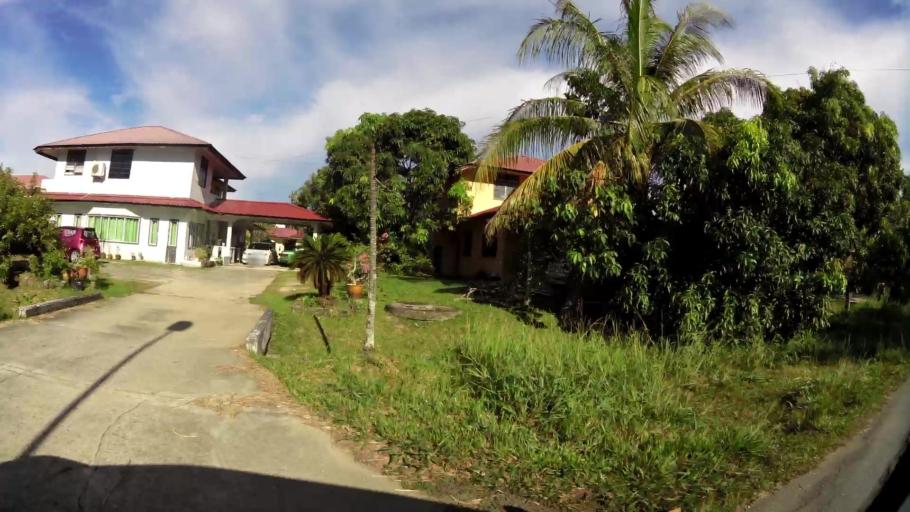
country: BN
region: Brunei and Muara
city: Bandar Seri Begawan
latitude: 4.9692
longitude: 114.9620
